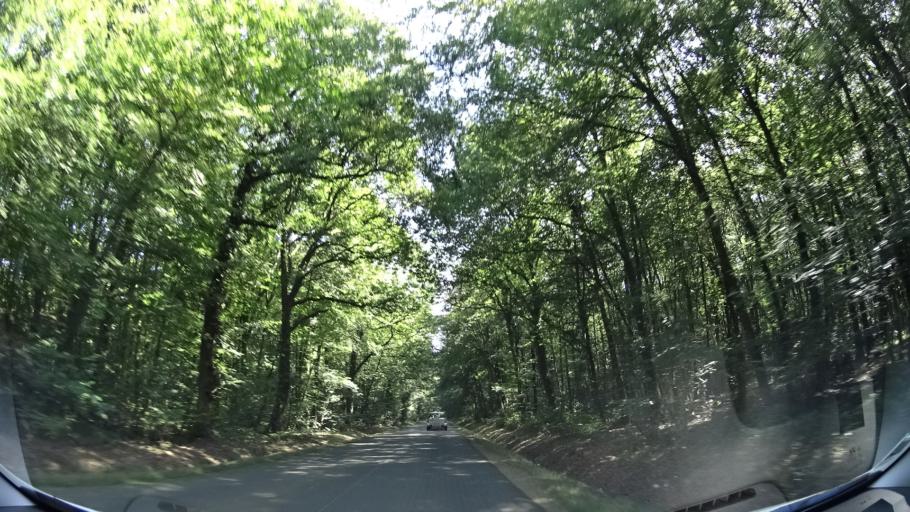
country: FR
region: Brittany
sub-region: Departement d'Ille-et-Vilaine
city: Saint-Sulpice-la-Foret
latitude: 48.2099
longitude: -1.5527
